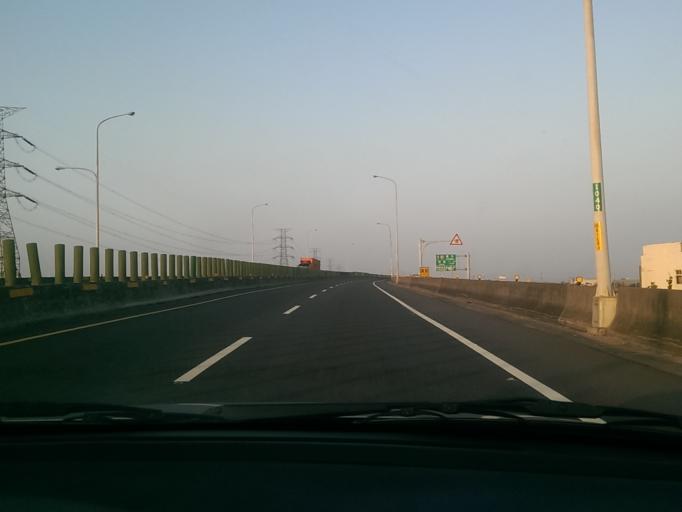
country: TW
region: Taiwan
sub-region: Changhua
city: Chang-hua
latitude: 24.1571
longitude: 120.4589
